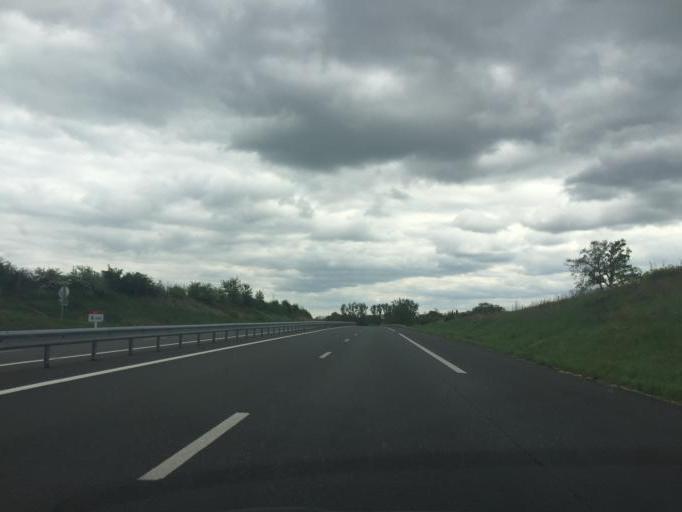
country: FR
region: Rhone-Alpes
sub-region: Departement de la Loire
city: La Pacaudiere
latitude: 46.1750
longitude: 3.8804
